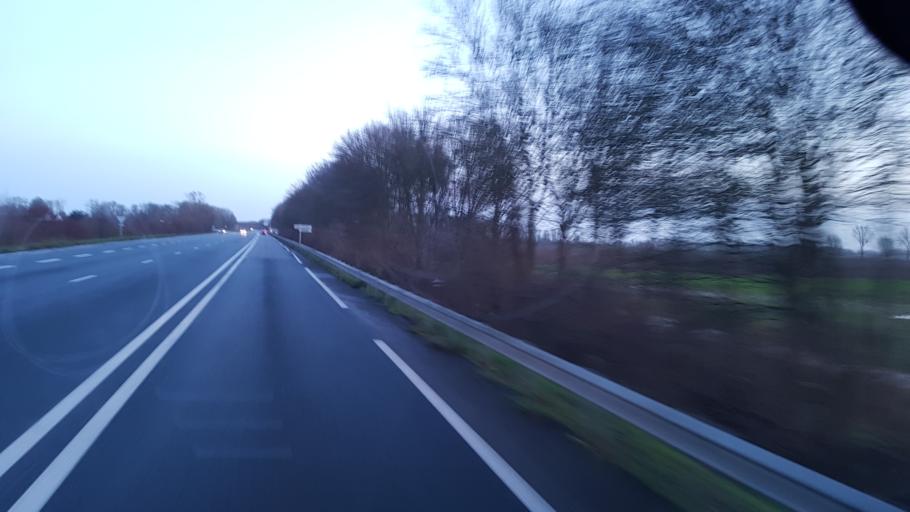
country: FR
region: Nord-Pas-de-Calais
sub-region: Departement du Nord
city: Ferin
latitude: 50.3392
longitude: 3.0836
